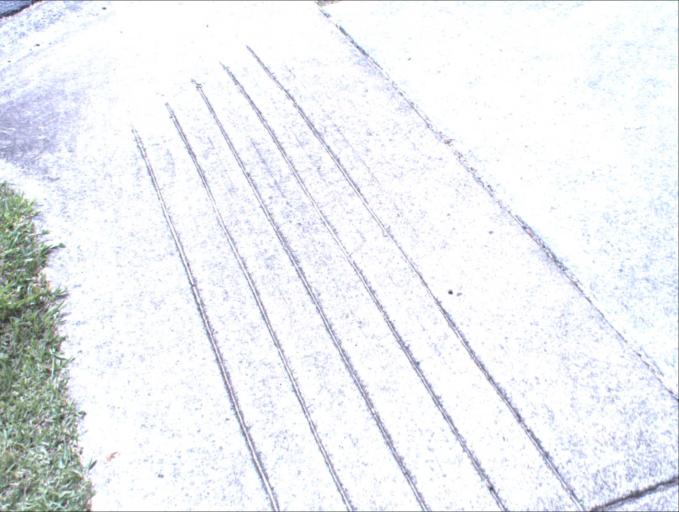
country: AU
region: Queensland
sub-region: Logan
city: Rochedale South
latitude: -27.5949
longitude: 153.1242
